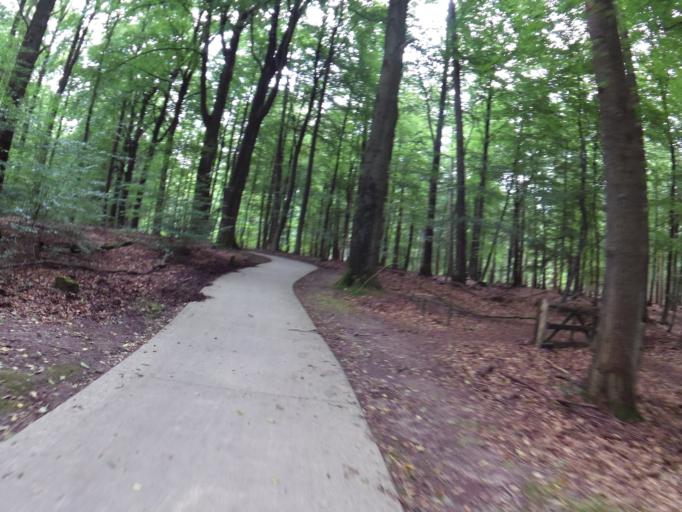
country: NL
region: Gelderland
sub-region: Gemeente Rheden
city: De Steeg
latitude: 52.0400
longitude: 6.0544
